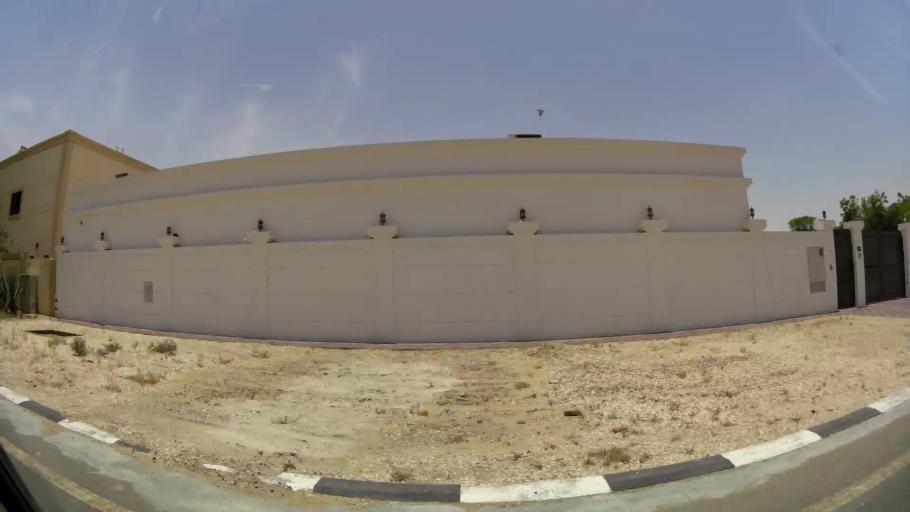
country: AE
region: Ash Shariqah
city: Sharjah
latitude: 25.2315
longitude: 55.4534
